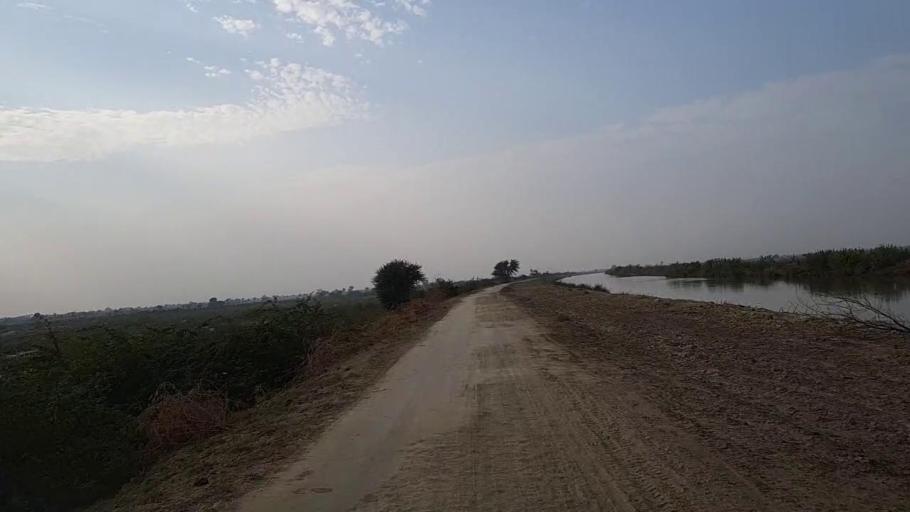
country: PK
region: Sindh
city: Pithoro
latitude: 25.4410
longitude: 69.2367
